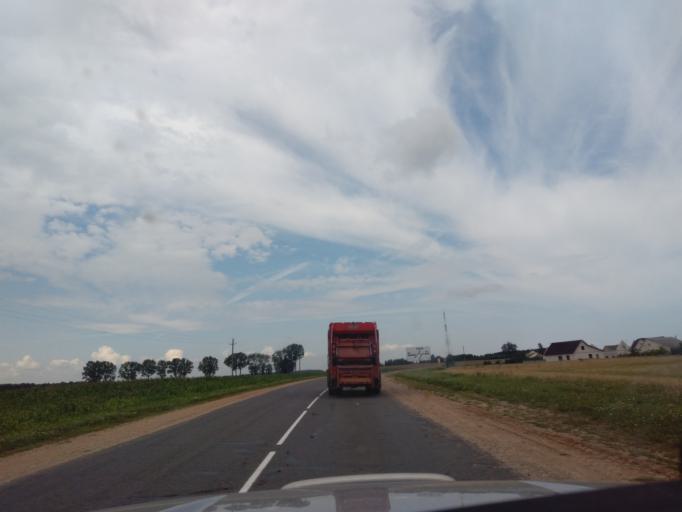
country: BY
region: Minsk
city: Kapyl'
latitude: 53.1353
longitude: 27.0935
